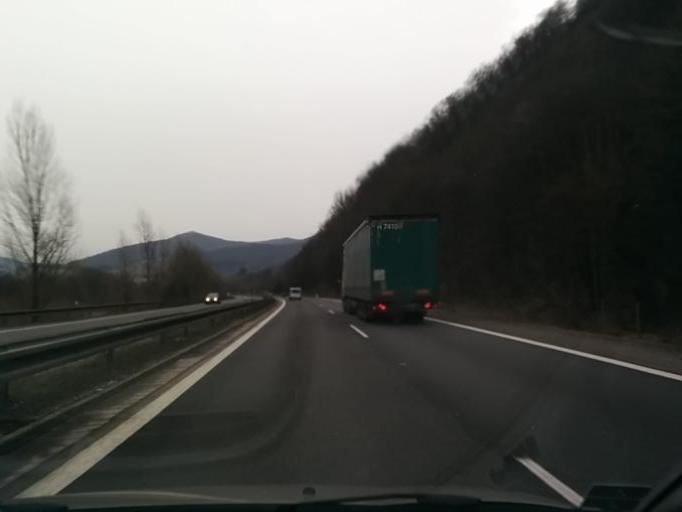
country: SK
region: Banskobystricky
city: Ziar nad Hronom
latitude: 48.5844
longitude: 18.9274
